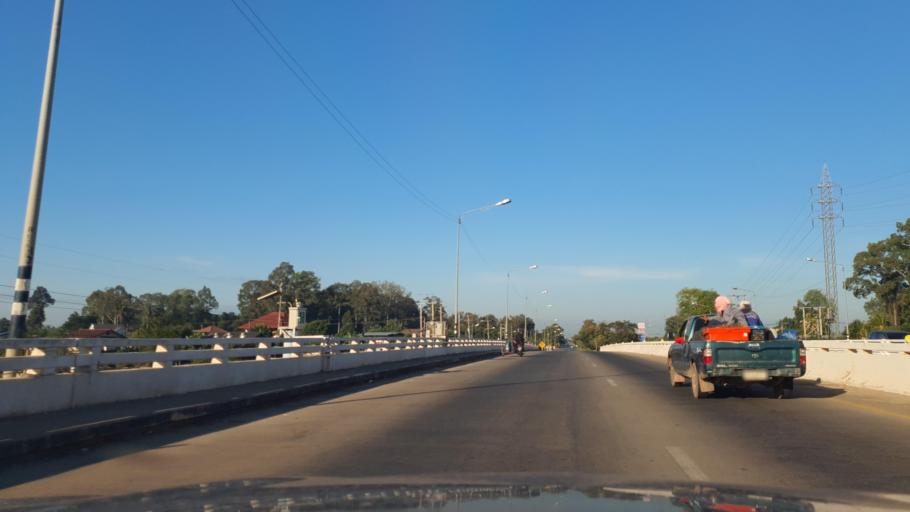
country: TH
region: Phitsanulok
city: Phitsanulok
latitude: 16.8648
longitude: 100.2452
